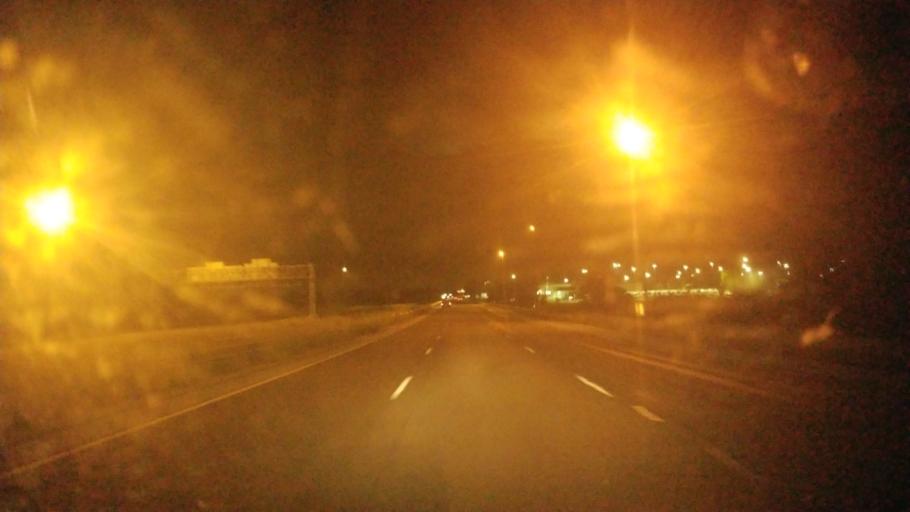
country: US
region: Illinois
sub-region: Madison County
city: Mitchell
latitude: 38.7578
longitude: -90.0707
